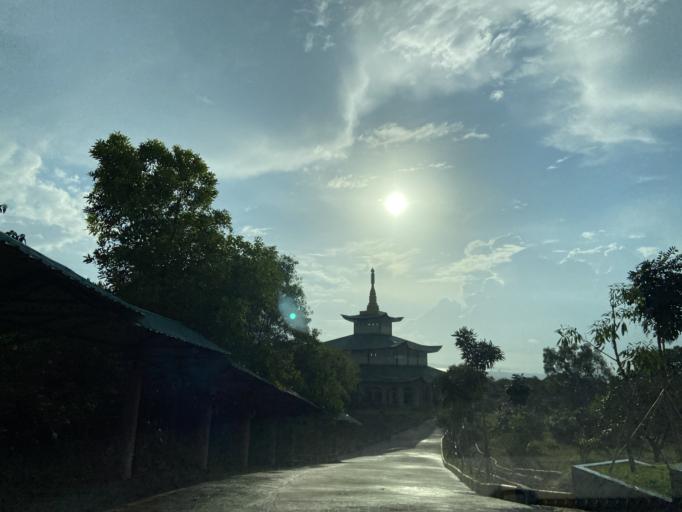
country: ID
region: Riau Islands
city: Tanjungpinang
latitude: 0.8918
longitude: 104.1225
